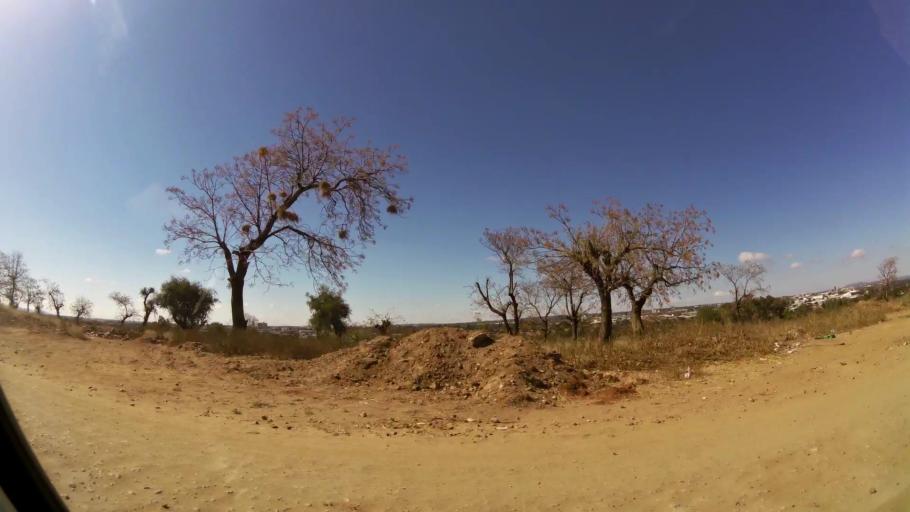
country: ZA
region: Limpopo
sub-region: Capricorn District Municipality
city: Polokwane
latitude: -23.8815
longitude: 29.4251
